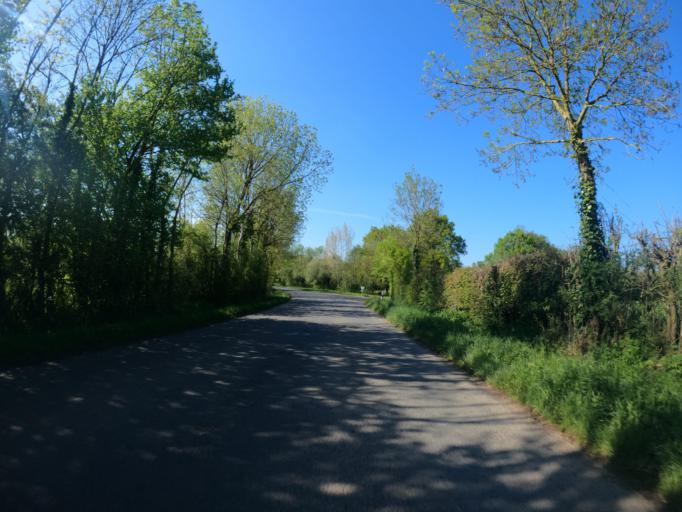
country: FR
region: Poitou-Charentes
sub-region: Departement des Deux-Sevres
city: Moncoutant
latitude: 46.7120
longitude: -0.5664
